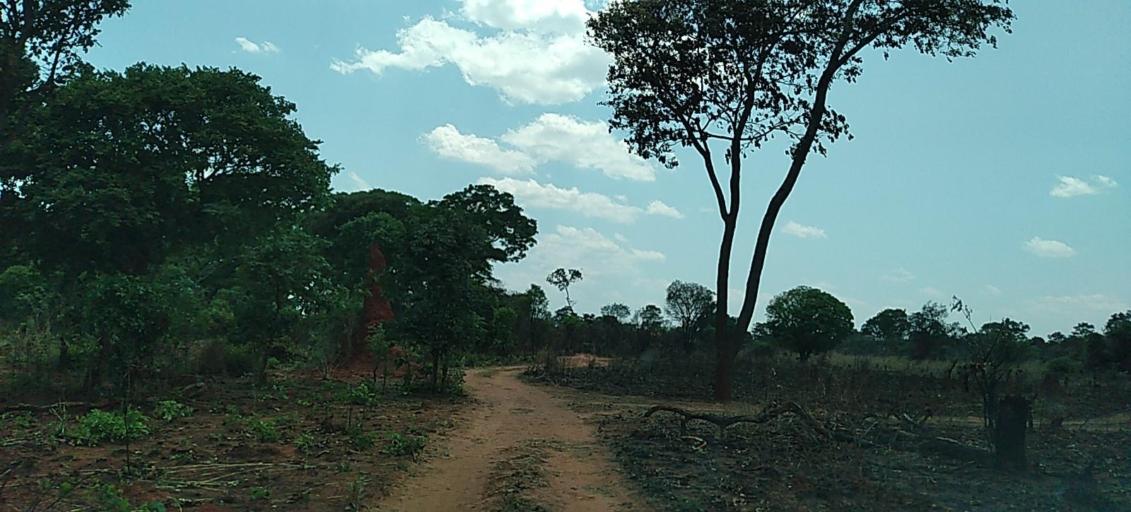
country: ZM
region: Central
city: Kapiri Mposhi
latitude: -13.6305
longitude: 28.7704
